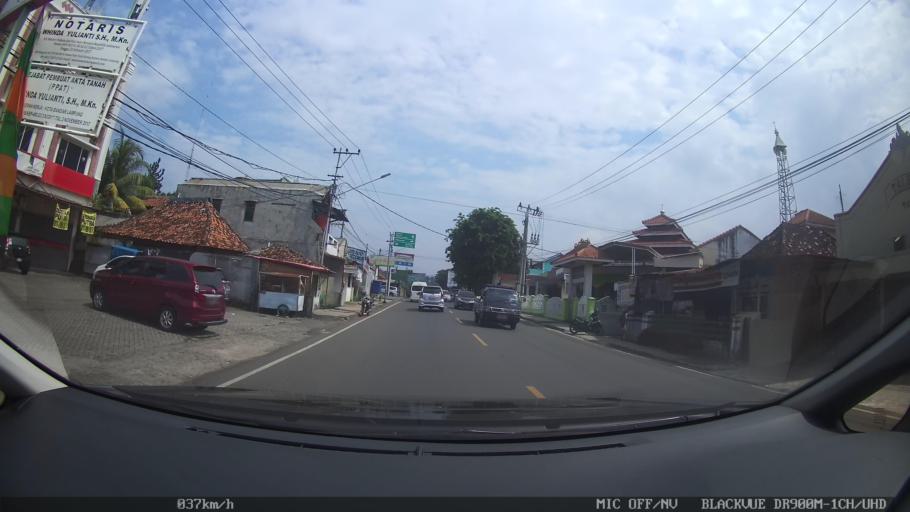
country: ID
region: Lampung
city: Bandarlampung
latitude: -5.4360
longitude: 105.2552
